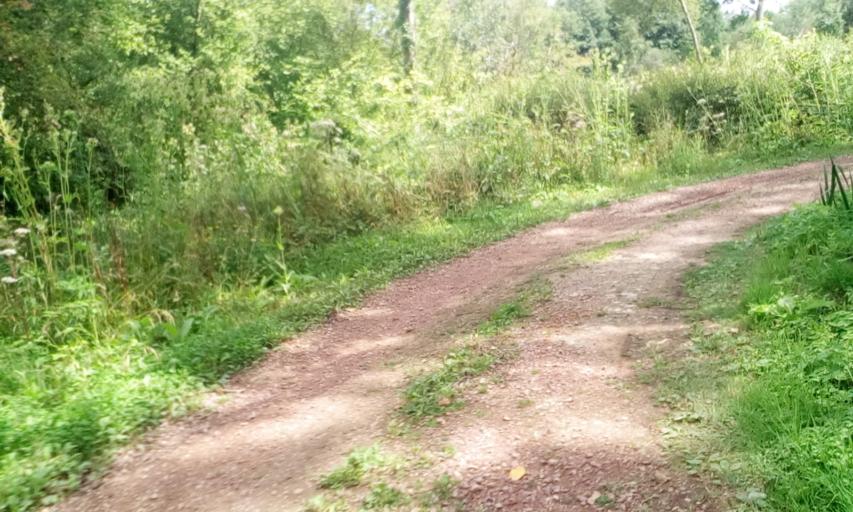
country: FR
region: Lower Normandy
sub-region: Departement du Calvados
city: Bellengreville
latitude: 49.1140
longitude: -0.2180
